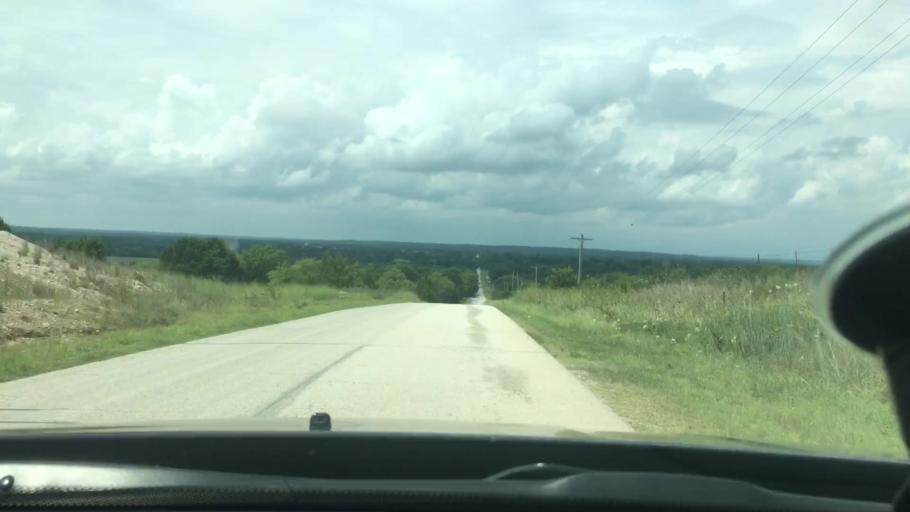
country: US
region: Oklahoma
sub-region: Carter County
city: Dickson
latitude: 34.2527
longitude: -96.9356
